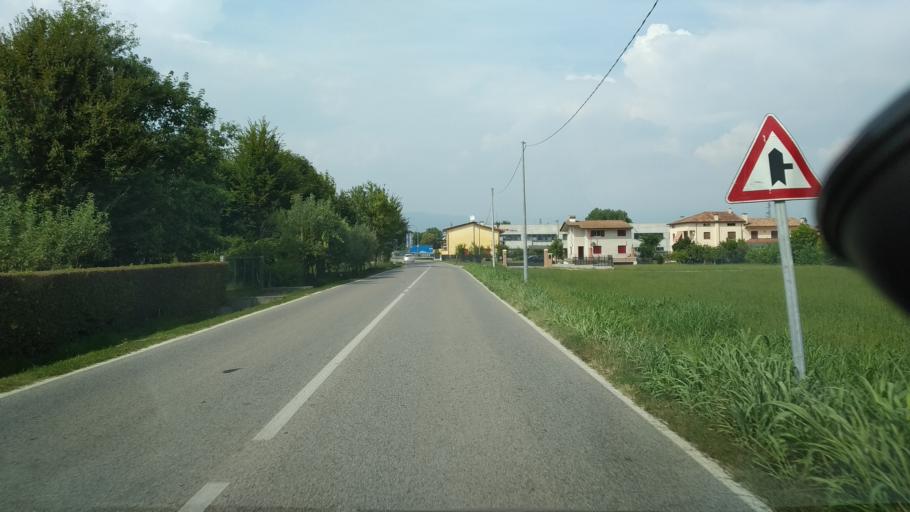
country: IT
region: Veneto
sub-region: Provincia di Vicenza
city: Pozzoleone
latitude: 45.6690
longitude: 11.6831
